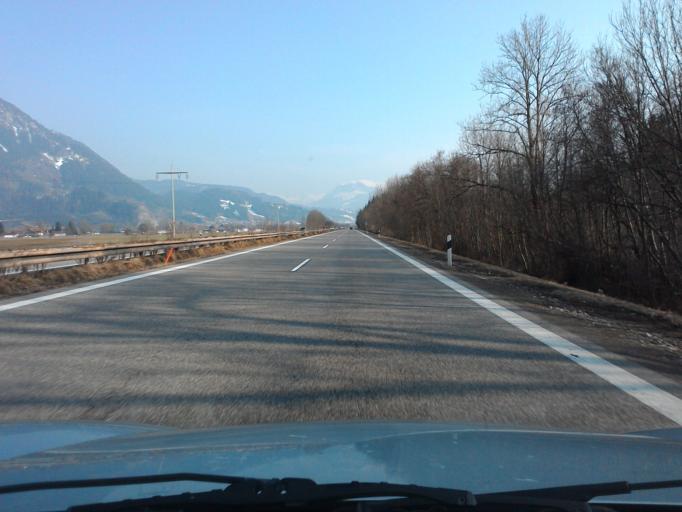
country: DE
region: Bavaria
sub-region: Swabia
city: Blaichach
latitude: 47.5538
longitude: 10.2542
